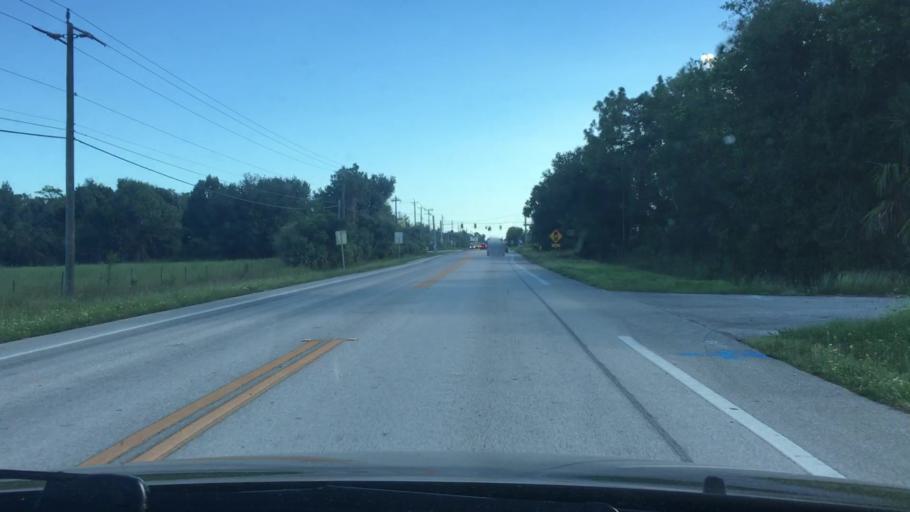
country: US
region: Florida
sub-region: Volusia County
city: Samsula-Spruce Creek
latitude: 29.0853
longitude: -81.0685
